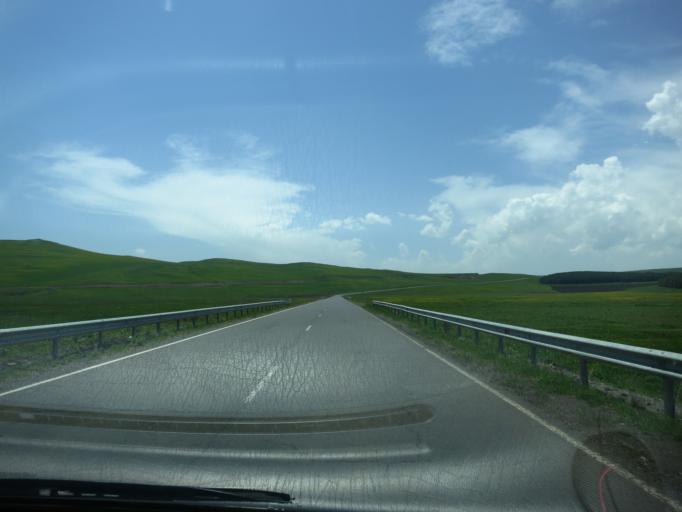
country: GE
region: Samtskhe-Javakheti
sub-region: Ninotsminda
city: Ninotsminda
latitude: 41.2969
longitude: 43.7531
